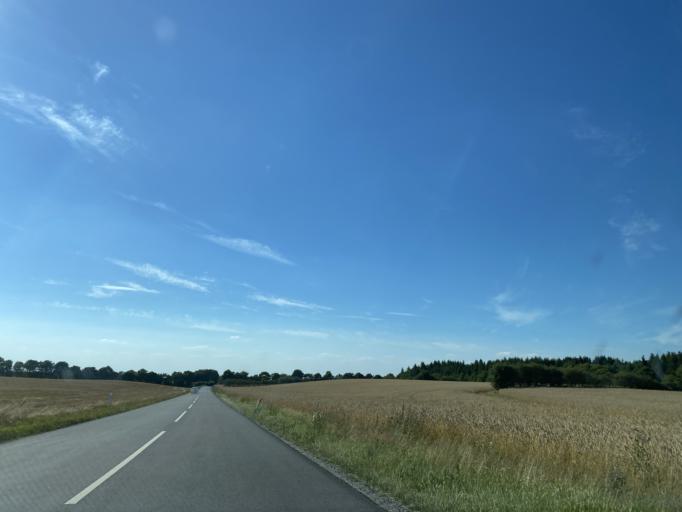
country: DK
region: South Denmark
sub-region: Vejle Kommune
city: Give
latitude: 55.8708
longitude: 9.3514
